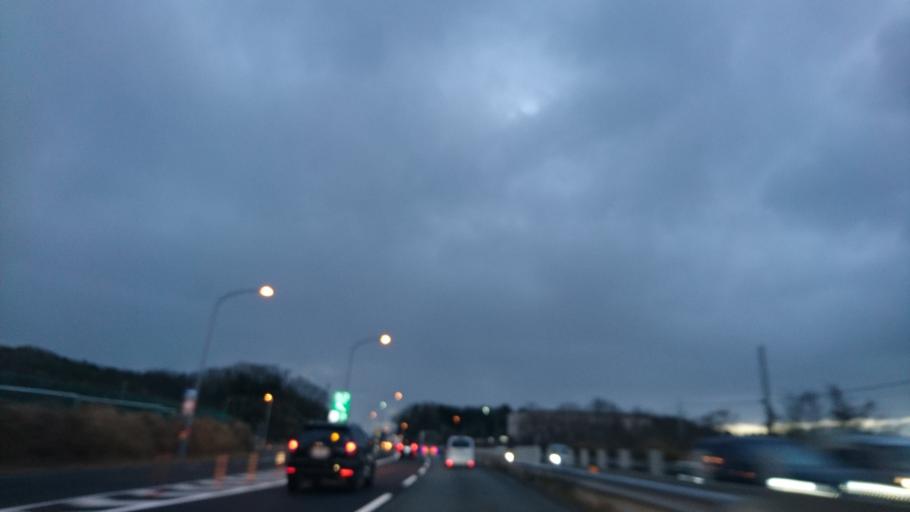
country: JP
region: Mie
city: Nabari
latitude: 34.6275
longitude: 135.9855
